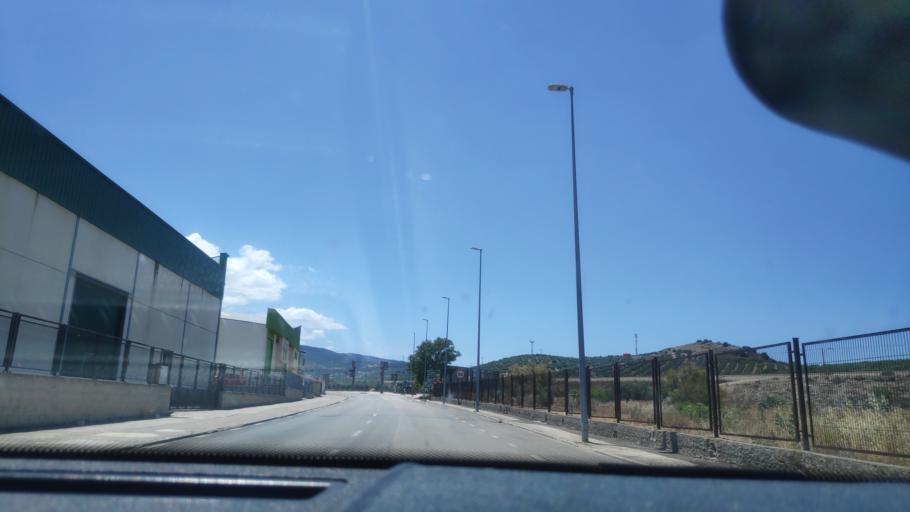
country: ES
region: Andalusia
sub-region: Provincia de Jaen
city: Jaen
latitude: 37.8031
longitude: -3.7866
